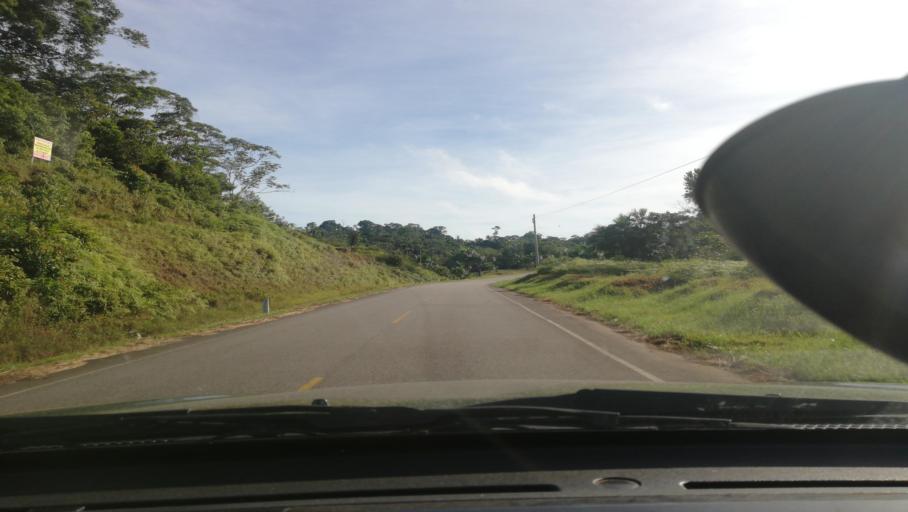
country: PE
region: Loreto
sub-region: Provincia de Loreto
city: Nauta
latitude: -4.3953
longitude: -73.5729
